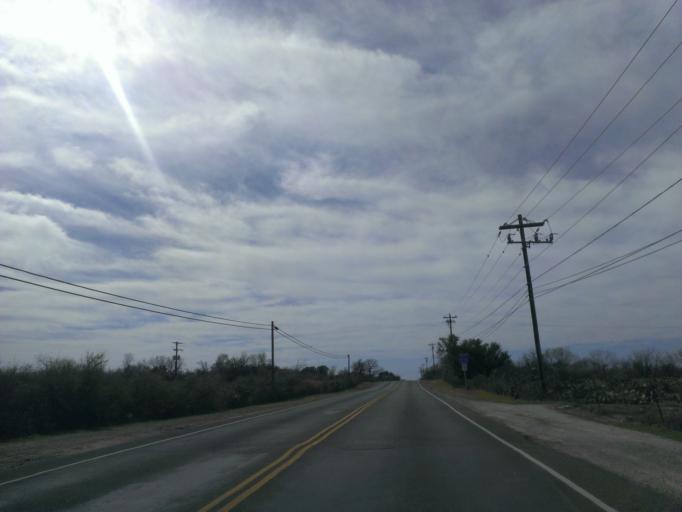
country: US
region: Texas
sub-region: Burnet County
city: Granite Shoals
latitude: 30.6043
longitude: -98.3719
